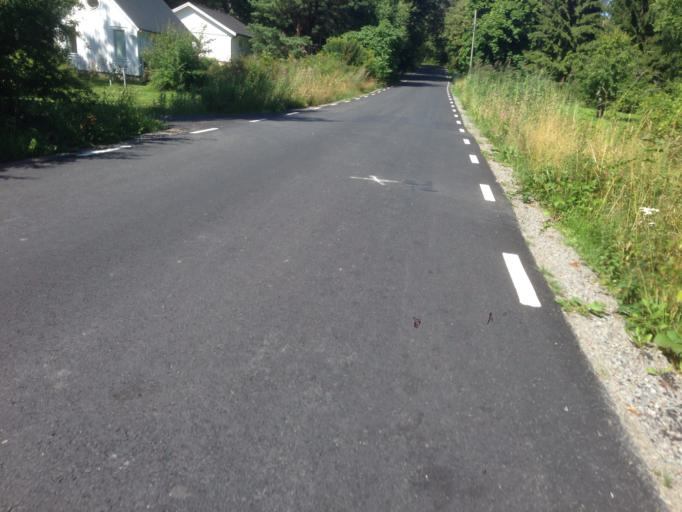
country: SE
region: Stockholm
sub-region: Vaxholms Kommun
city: Vaxholm
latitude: 59.3817
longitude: 18.3733
